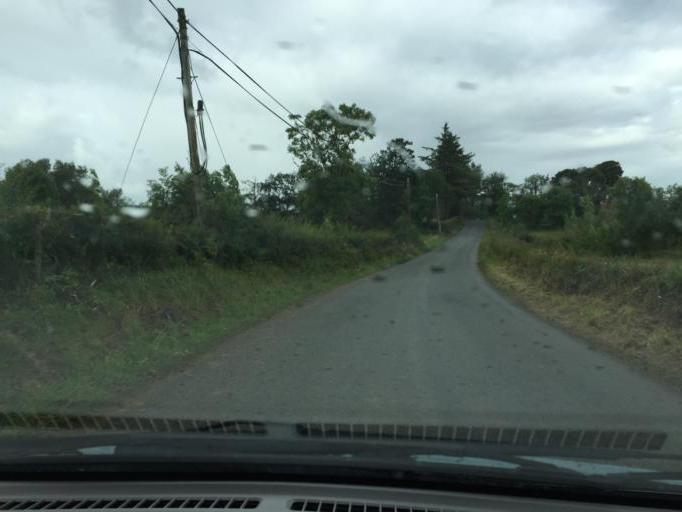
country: IE
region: Connaught
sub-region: Sligo
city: Tobercurry
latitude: 54.0384
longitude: -8.8564
